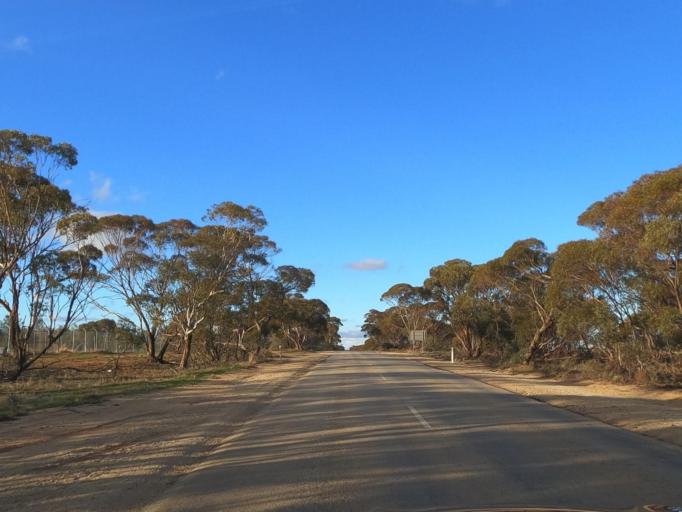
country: AU
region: Victoria
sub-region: Swan Hill
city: Swan Hill
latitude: -35.3495
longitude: 143.5121
